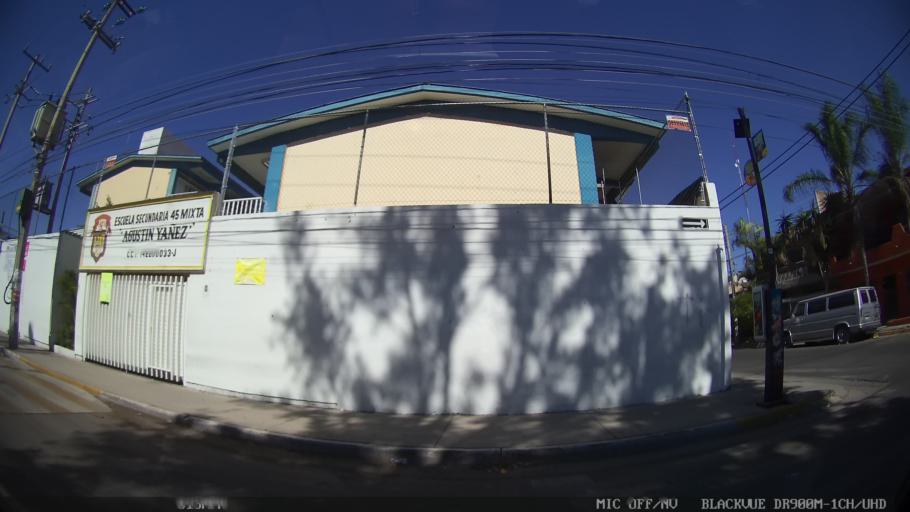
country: MX
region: Jalisco
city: Tlaquepaque
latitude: 20.6604
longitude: -103.2900
